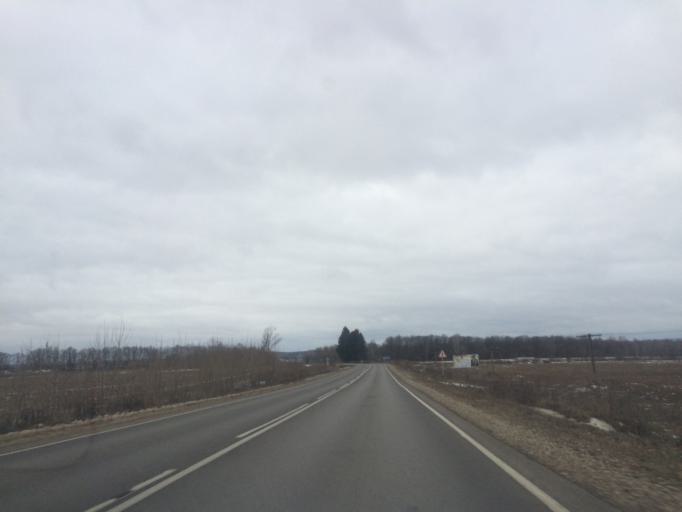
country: RU
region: Tula
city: Krapivna
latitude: 54.1144
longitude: 37.1574
